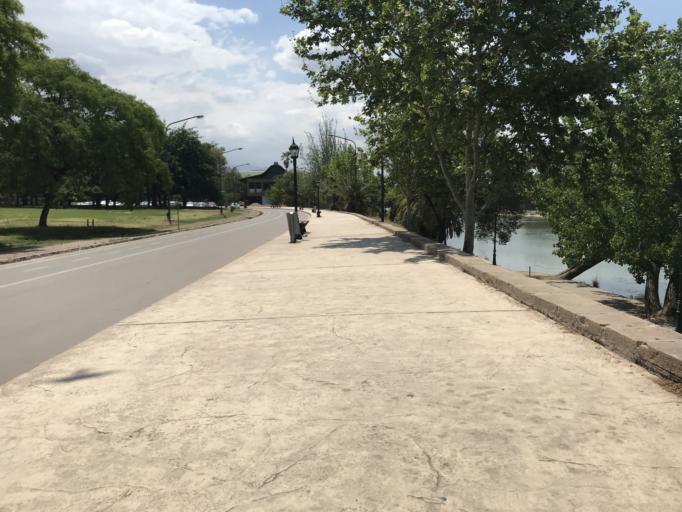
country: AR
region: Mendoza
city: Mendoza
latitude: -32.8954
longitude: -68.8658
